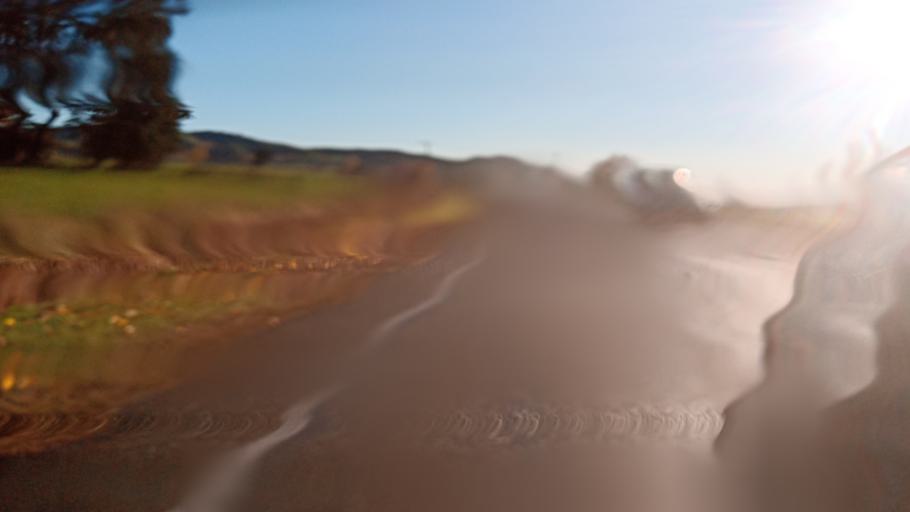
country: NZ
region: Hawke's Bay
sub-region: Wairoa District
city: Wairoa
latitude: -39.0251
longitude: 177.3746
